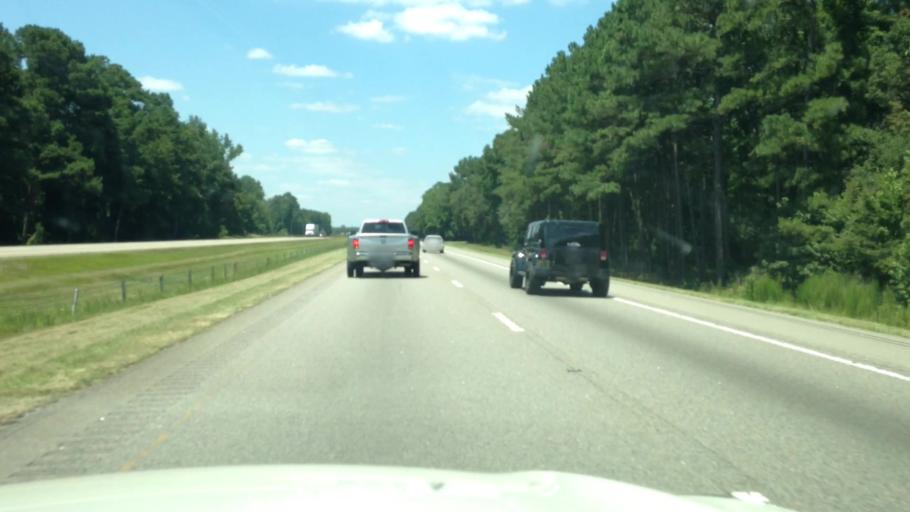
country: US
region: North Carolina
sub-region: Robeson County
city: Saint Pauls
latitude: 34.7796
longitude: -78.9953
